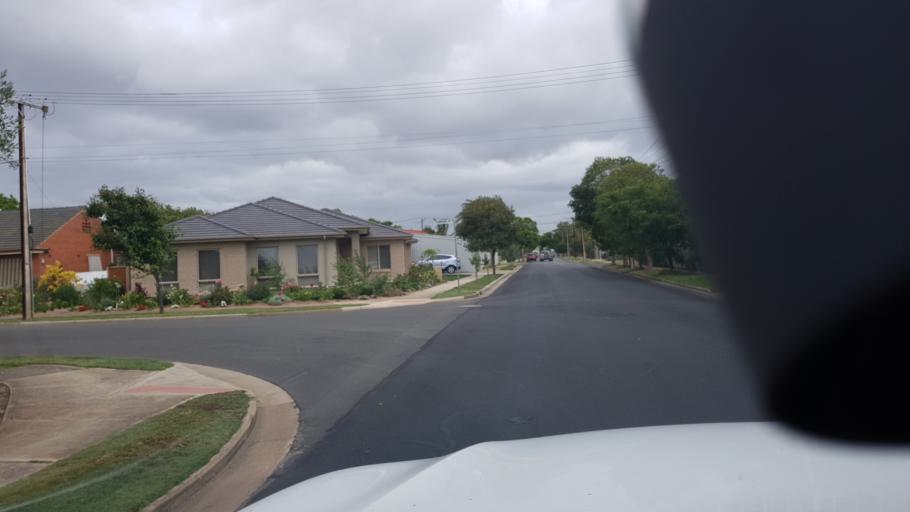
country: AU
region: South Australia
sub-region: Holdfast Bay
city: Glenelg East
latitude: -34.9654
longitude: 138.5231
